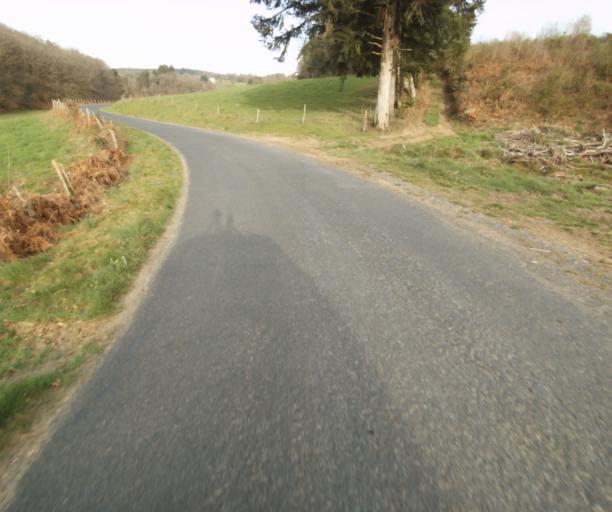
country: FR
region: Limousin
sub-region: Departement de la Correze
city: Chamboulive
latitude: 45.4449
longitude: 1.7626
